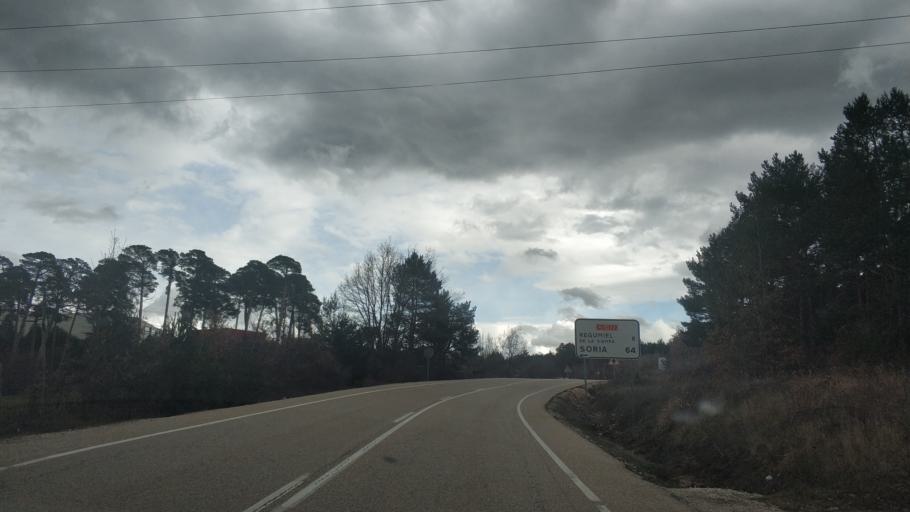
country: ES
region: Castille and Leon
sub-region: Provincia de Burgos
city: Quintanar de la Sierra
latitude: 41.9722
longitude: -3.0412
